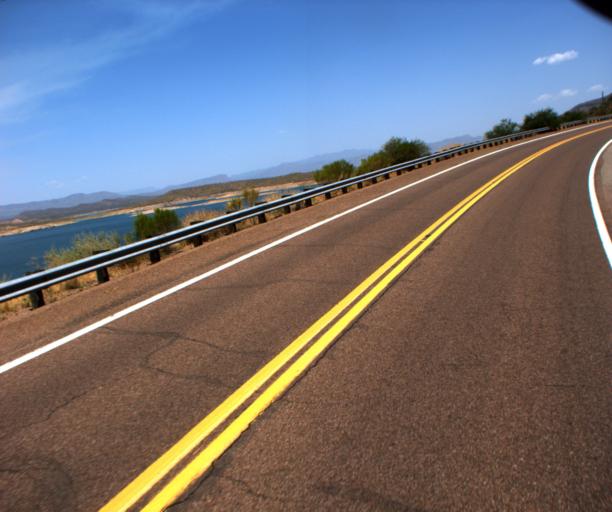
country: US
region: Arizona
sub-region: Gila County
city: Tonto Basin
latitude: 33.6940
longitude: -111.1770
